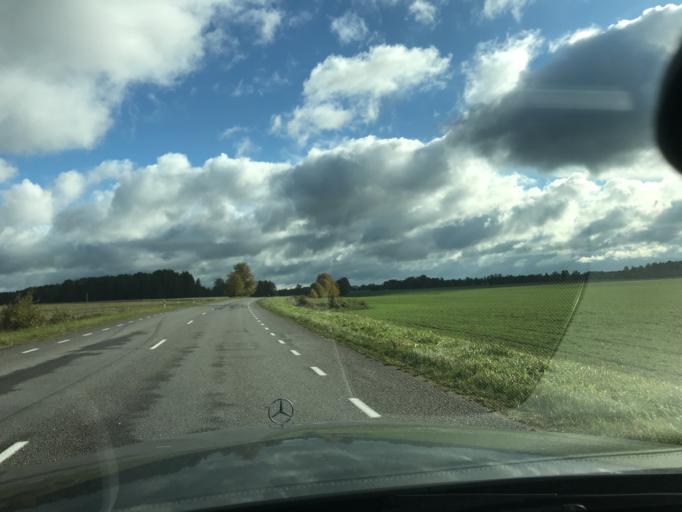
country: EE
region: Valgamaa
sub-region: Torva linn
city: Torva
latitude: 57.9791
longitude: 25.9671
